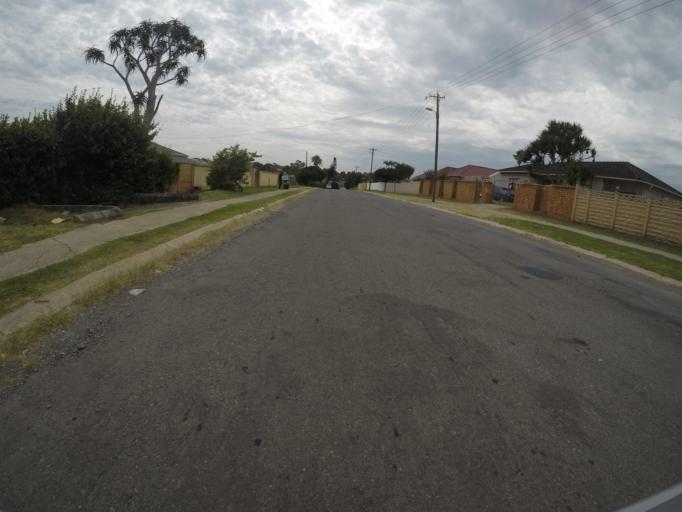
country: ZA
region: Eastern Cape
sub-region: Buffalo City Metropolitan Municipality
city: East London
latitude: -32.9976
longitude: 27.8739
